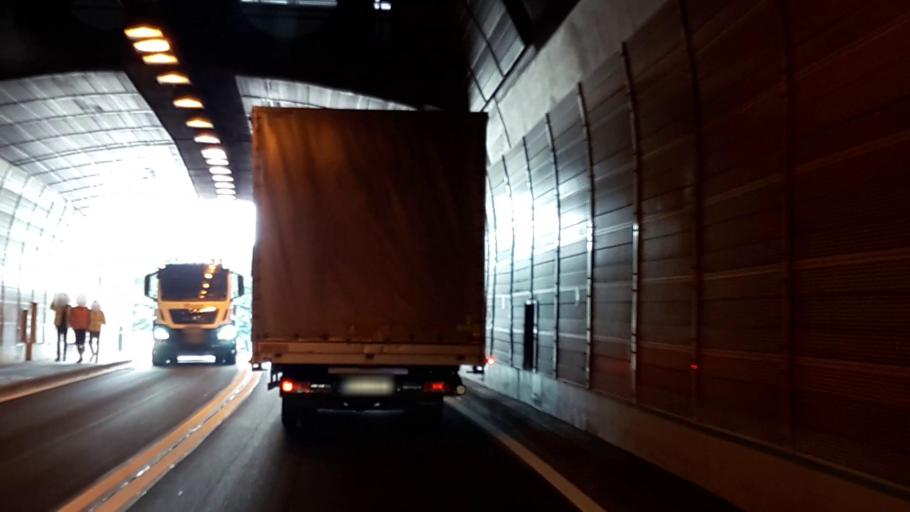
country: AT
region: Upper Austria
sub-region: Linz Stadt
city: Linz
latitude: 48.3039
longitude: 14.2811
